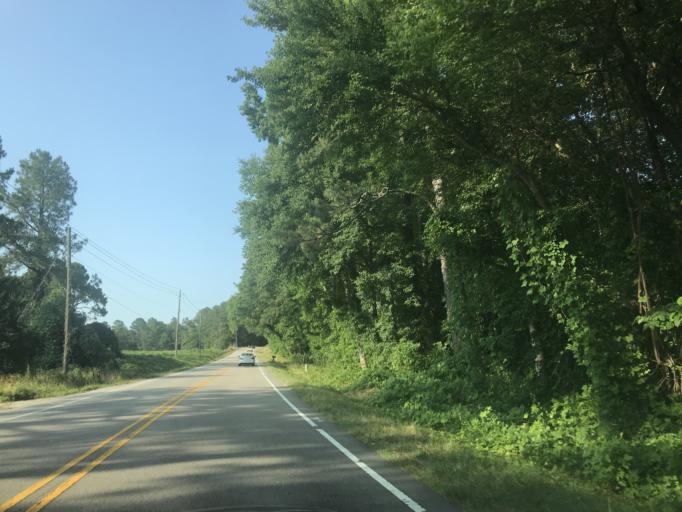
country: US
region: North Carolina
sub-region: Wake County
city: Knightdale
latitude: 35.8579
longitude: -78.4956
